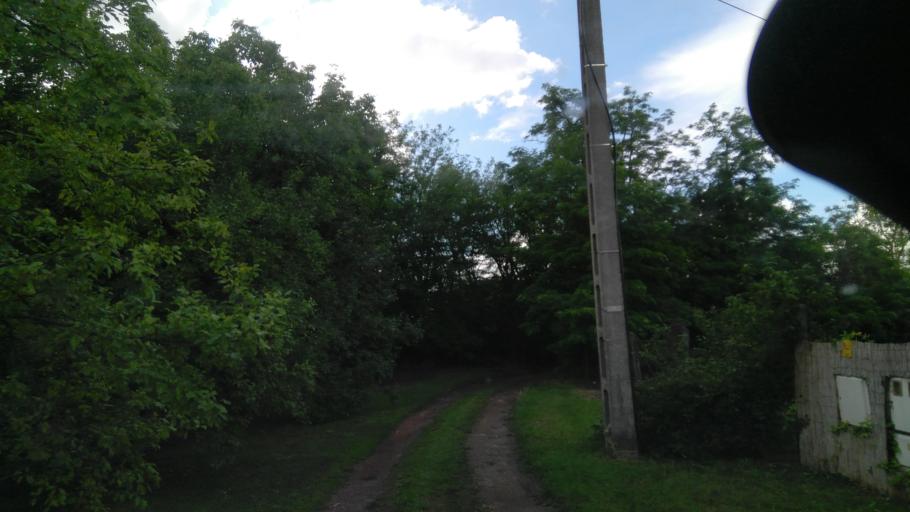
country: HU
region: Bekes
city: Doboz
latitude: 46.6990
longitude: 21.1805
